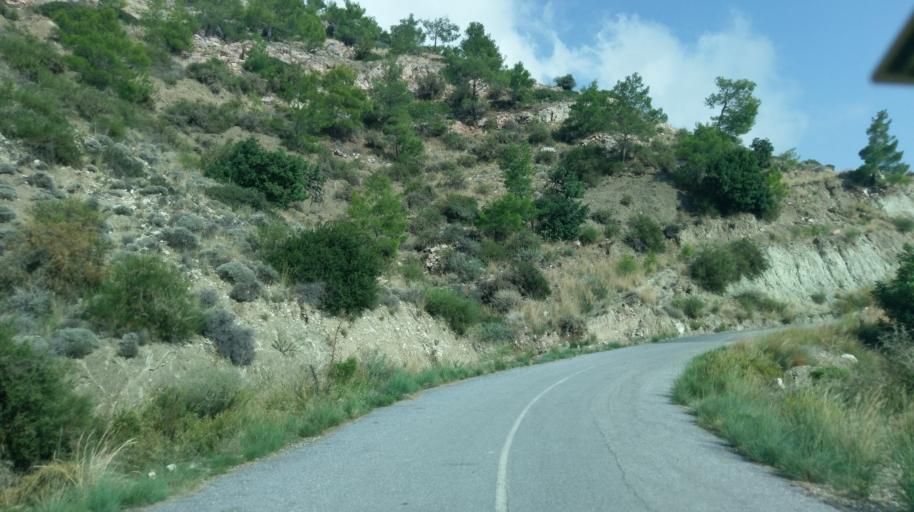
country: CY
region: Ammochostos
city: Lefkonoiko
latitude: 35.3073
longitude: 33.6053
